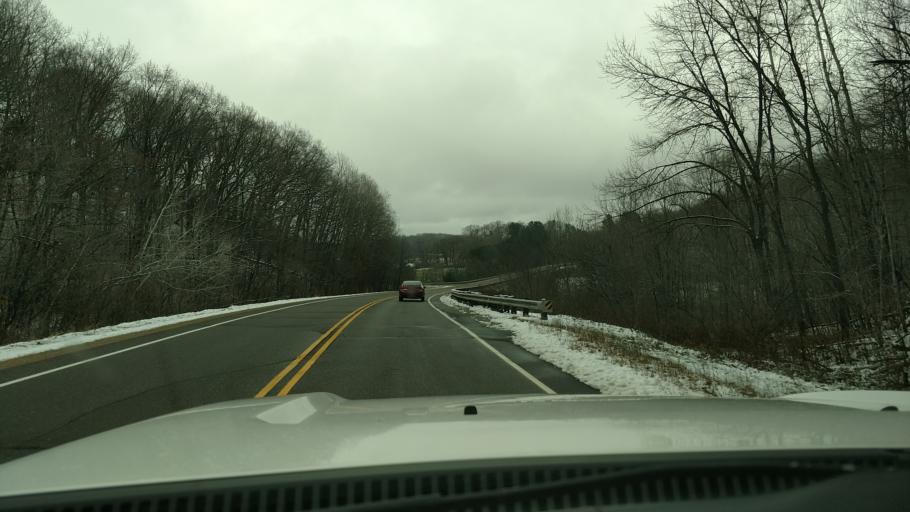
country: US
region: Wisconsin
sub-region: Dunn County
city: Boyceville
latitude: 45.1376
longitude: -91.9849
